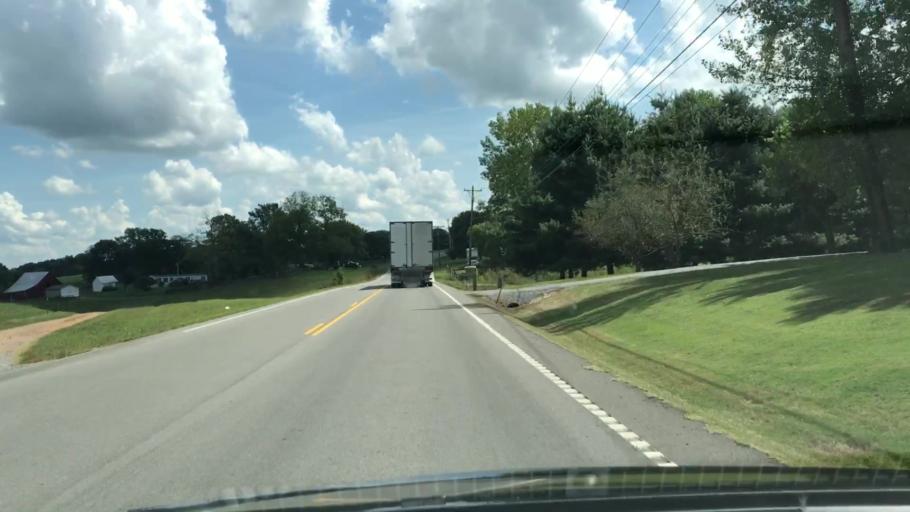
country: US
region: Tennessee
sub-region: Robertson County
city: Cross Plains
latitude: 36.5356
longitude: -86.6553
